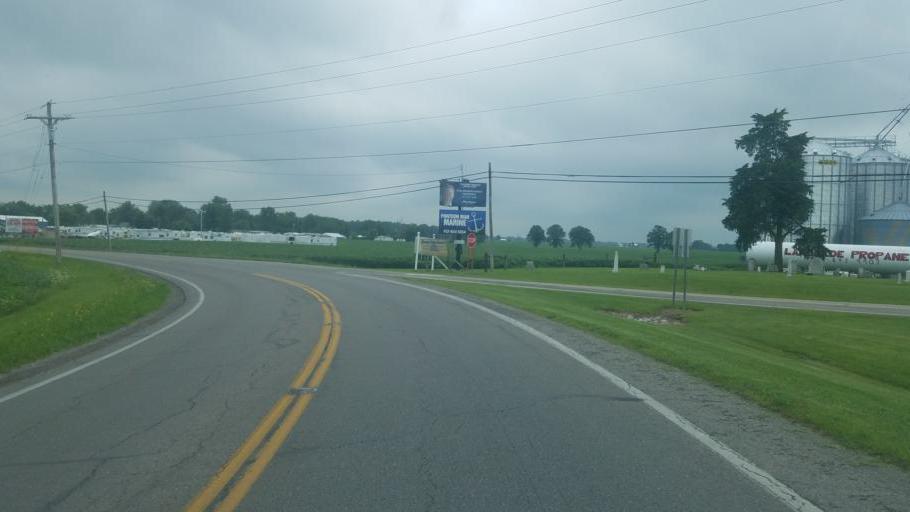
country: US
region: Ohio
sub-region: Logan County
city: Lakeview
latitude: 40.5147
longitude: -83.9174
